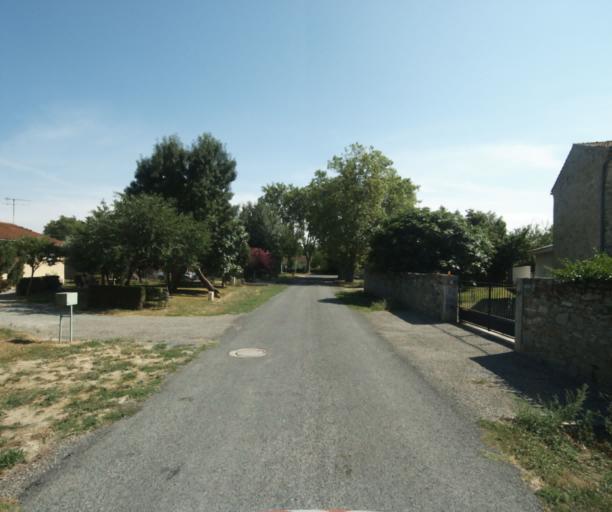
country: FR
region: Midi-Pyrenees
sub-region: Departement de la Haute-Garonne
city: Revel
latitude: 43.4952
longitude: 1.9696
